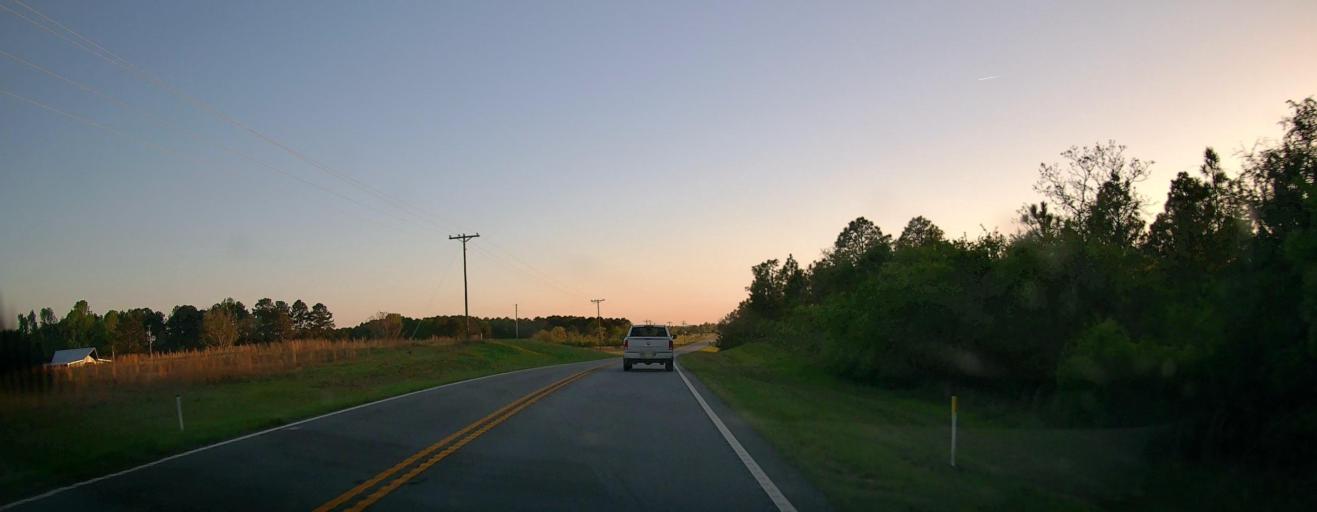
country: US
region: Georgia
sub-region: Marion County
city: Buena Vista
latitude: 32.4928
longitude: -84.6164
